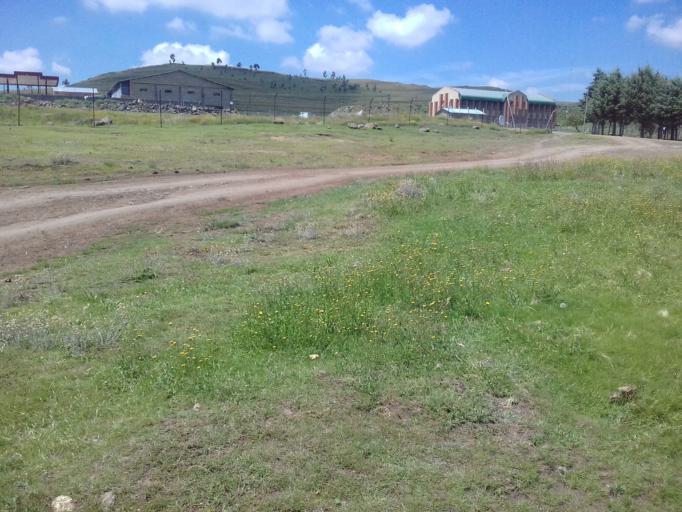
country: LS
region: Thaba-Tseka
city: Thaba-Tseka
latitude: -29.5231
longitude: 28.6034
